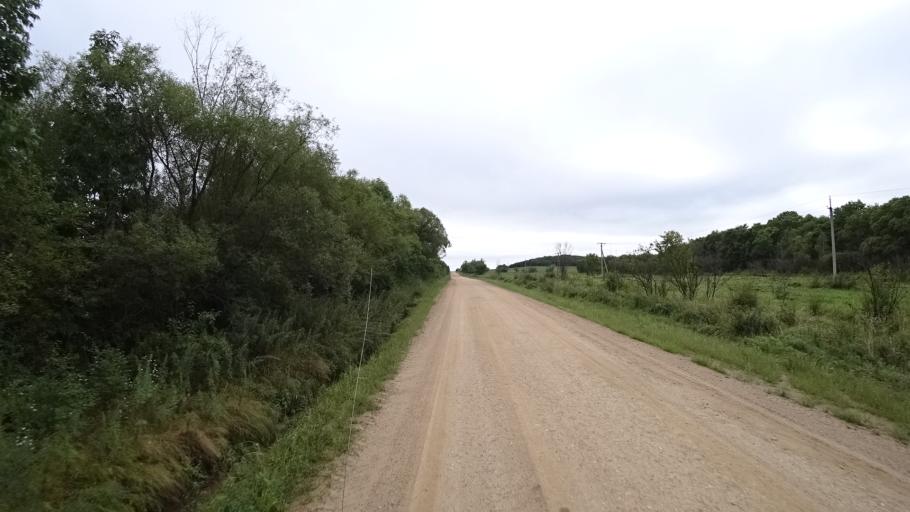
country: RU
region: Primorskiy
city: Monastyrishche
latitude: 44.0983
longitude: 132.6023
